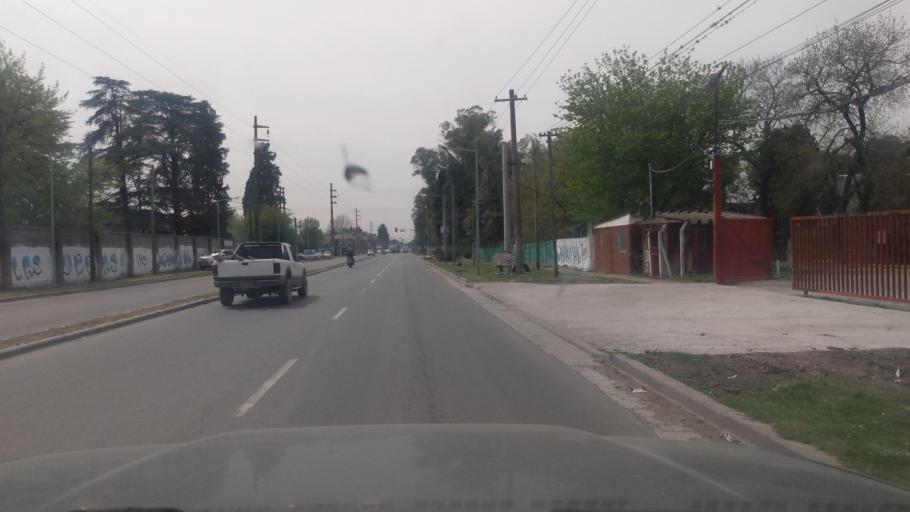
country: AR
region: Buenos Aires
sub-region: Partido de Pilar
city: Pilar
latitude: -34.4395
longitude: -58.8957
